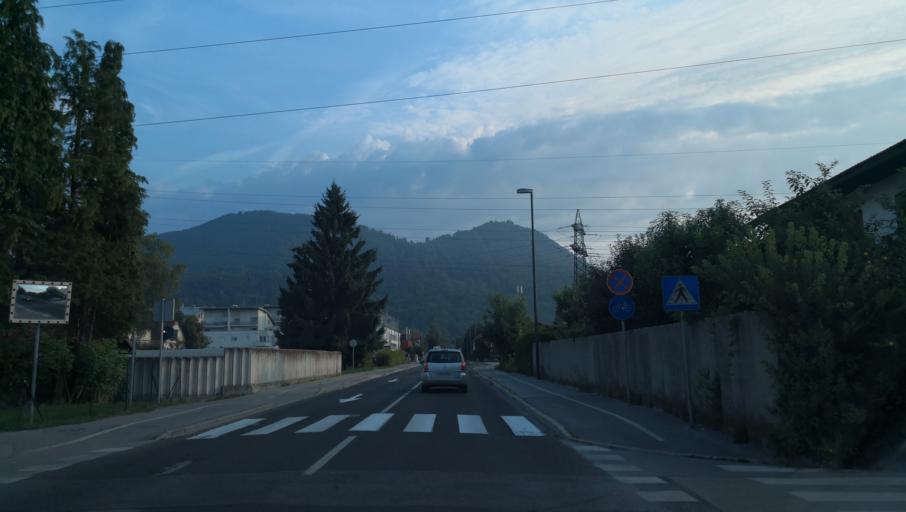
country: SI
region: Medvode
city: Zgornje Pirnice
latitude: 46.1115
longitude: 14.4618
